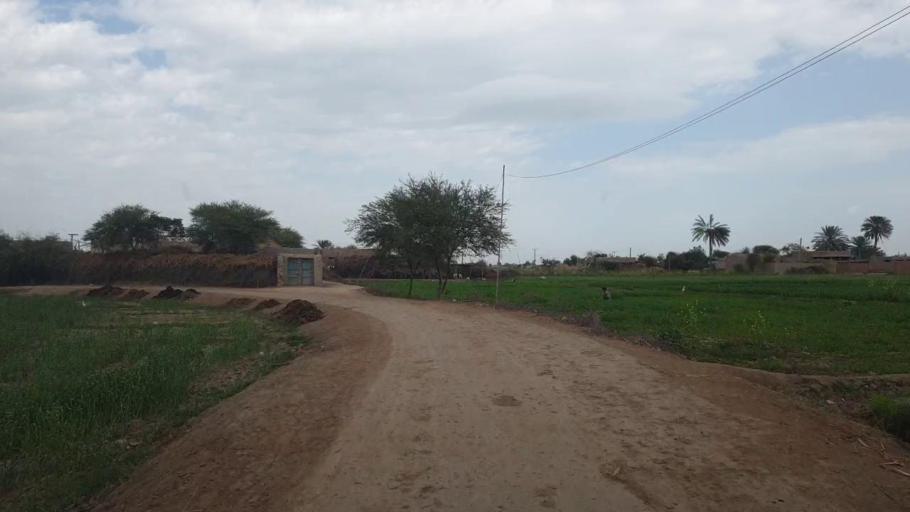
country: PK
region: Sindh
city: Hala
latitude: 25.9810
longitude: 68.4165
